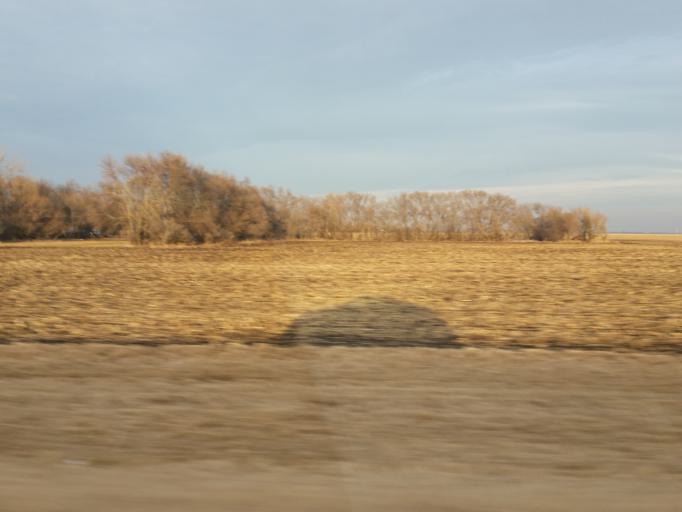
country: US
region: North Dakota
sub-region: Traill County
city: Mayville
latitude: 47.4674
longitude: -97.3261
